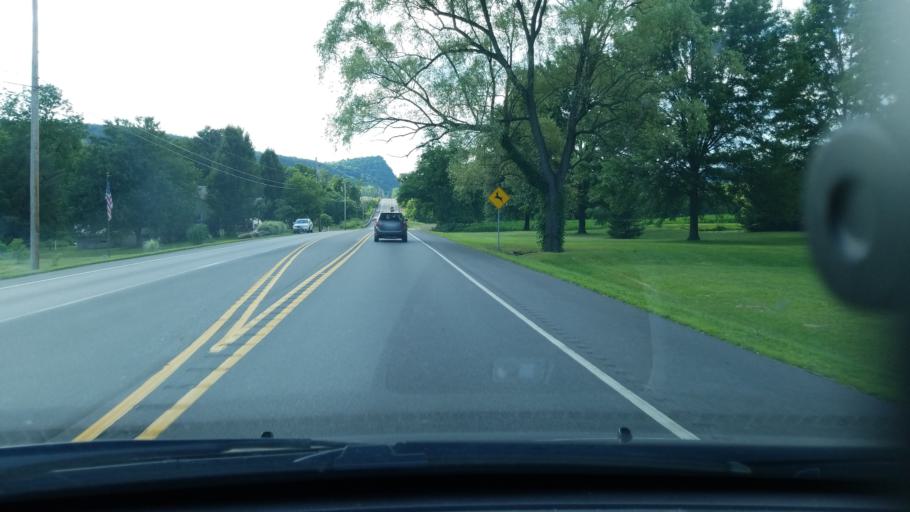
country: US
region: Pennsylvania
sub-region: Montour County
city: Mechanicsville
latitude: 40.9309
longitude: -76.5923
